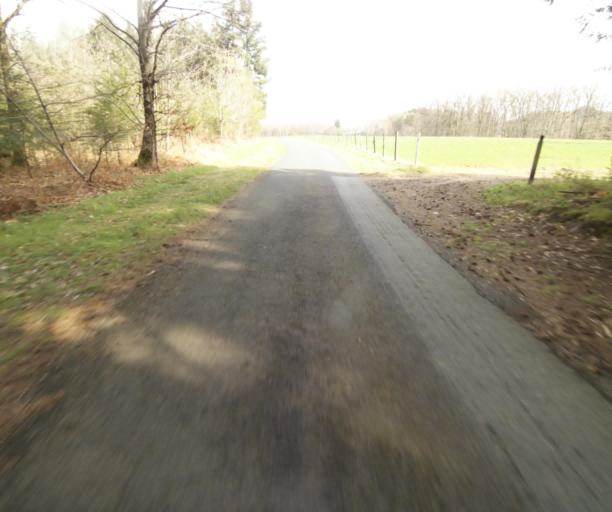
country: FR
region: Limousin
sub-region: Departement de la Correze
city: Correze
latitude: 45.3523
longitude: 1.8974
